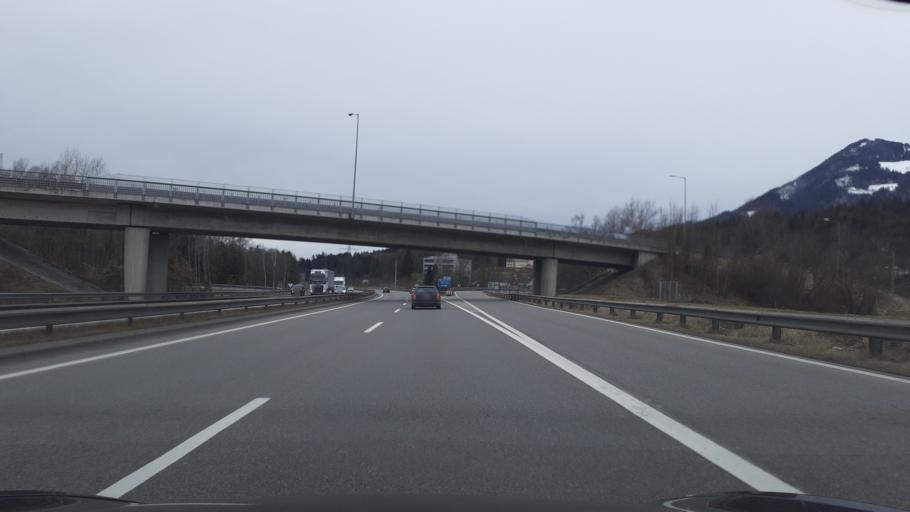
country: AT
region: Vorarlberg
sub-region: Politischer Bezirk Bludenz
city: Nenzing
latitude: 47.1907
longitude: 9.7182
